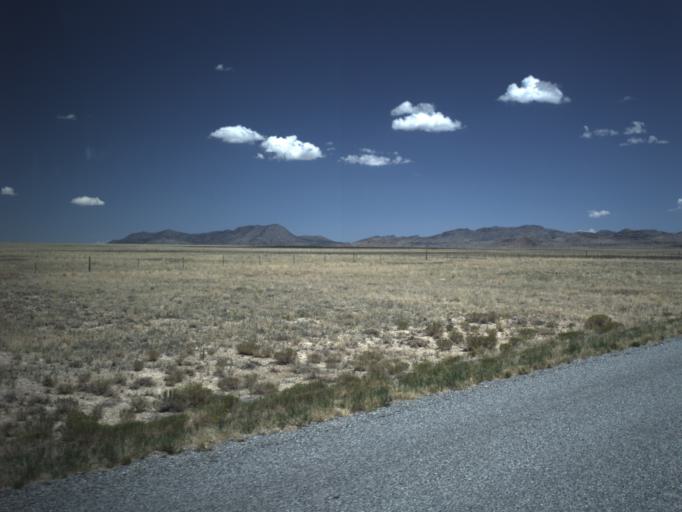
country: US
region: Utah
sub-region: Beaver County
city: Milford
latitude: 39.0457
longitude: -113.7977
